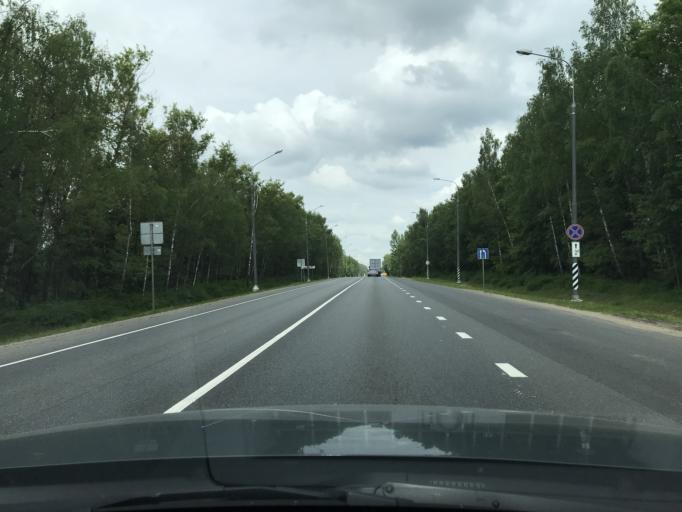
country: RU
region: Moskovskaya
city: Dorokhovo
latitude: 55.3773
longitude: 36.4049
